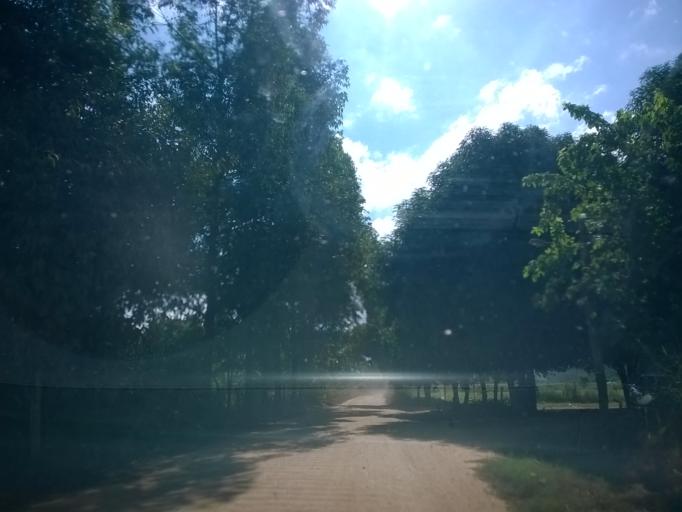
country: BR
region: Minas Gerais
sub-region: Uba
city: Uba
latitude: -21.0612
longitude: -42.9020
